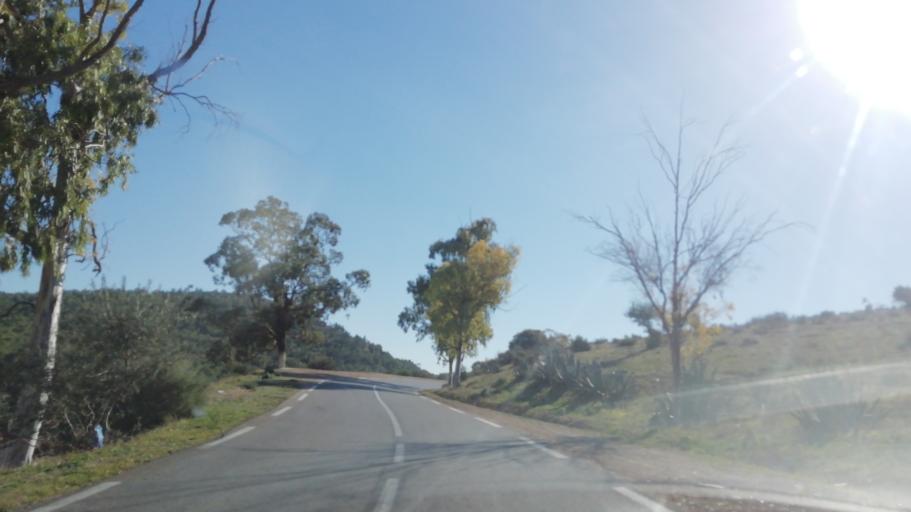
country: DZ
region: Tlemcen
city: Beni Mester
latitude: 34.8220
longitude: -1.6372
